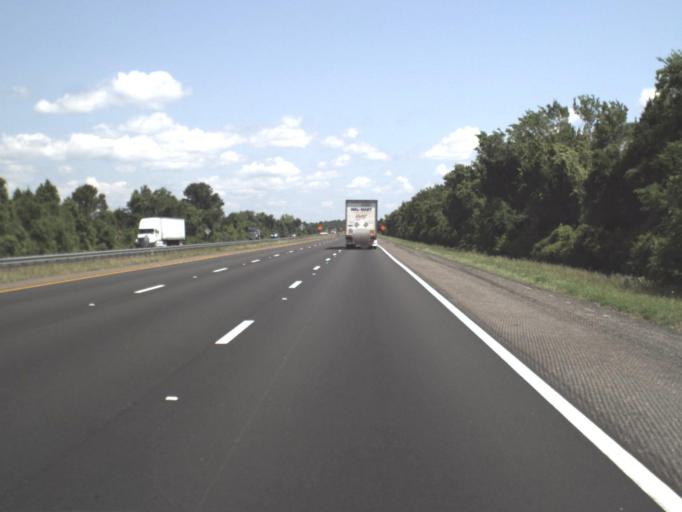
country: US
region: Florida
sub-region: Nassau County
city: Yulee
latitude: 30.5677
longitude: -81.6438
